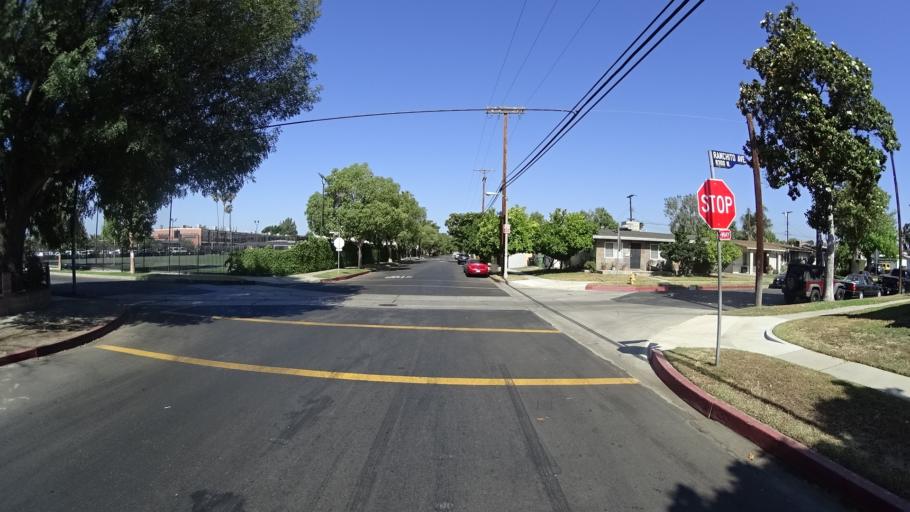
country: US
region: California
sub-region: Los Angeles County
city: Van Nuys
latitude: 34.2226
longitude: -118.4364
